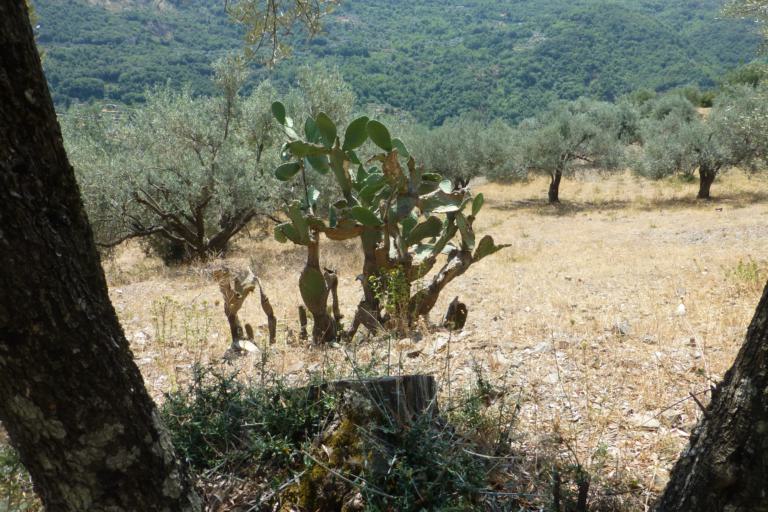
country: IT
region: Calabria
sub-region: Provincia di Reggio Calabria
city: Pazzano
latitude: 38.4784
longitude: 16.4360
